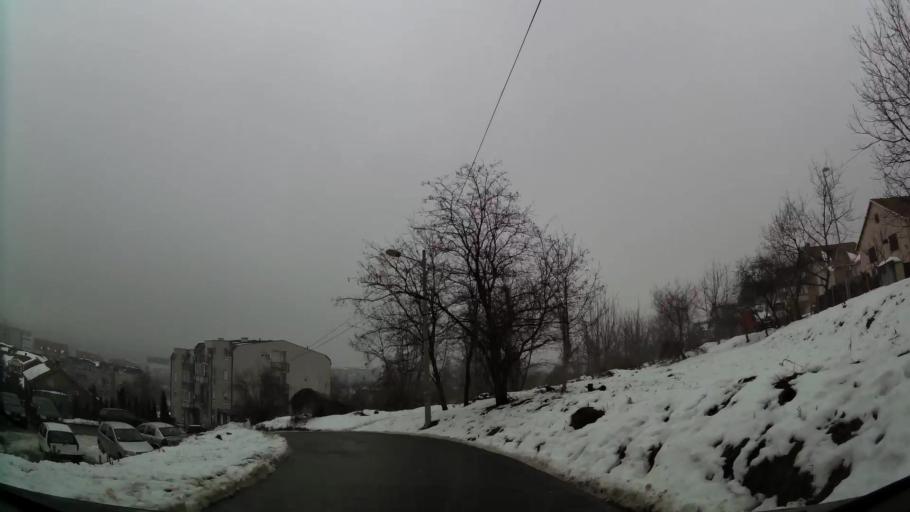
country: RS
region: Central Serbia
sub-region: Belgrade
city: Zvezdara
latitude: 44.7849
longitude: 20.5279
